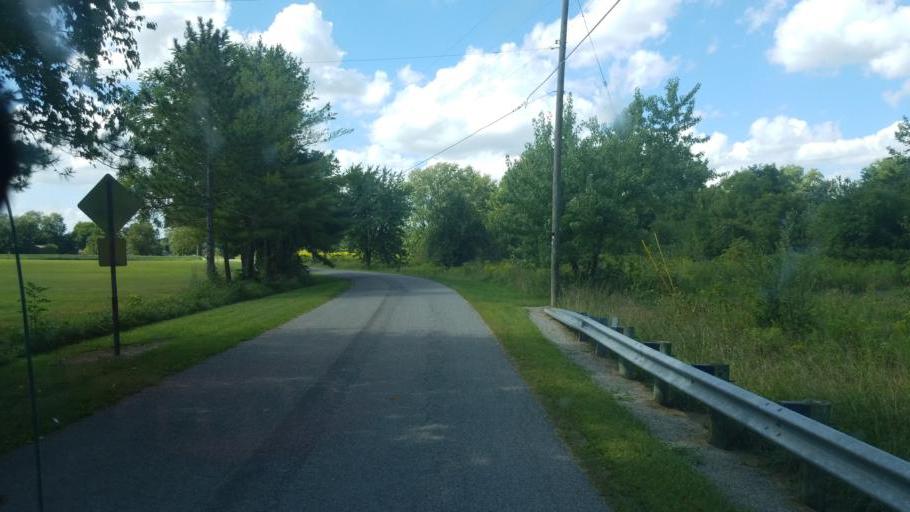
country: US
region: Ohio
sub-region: Union County
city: Richwood
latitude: 40.3471
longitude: -83.2538
